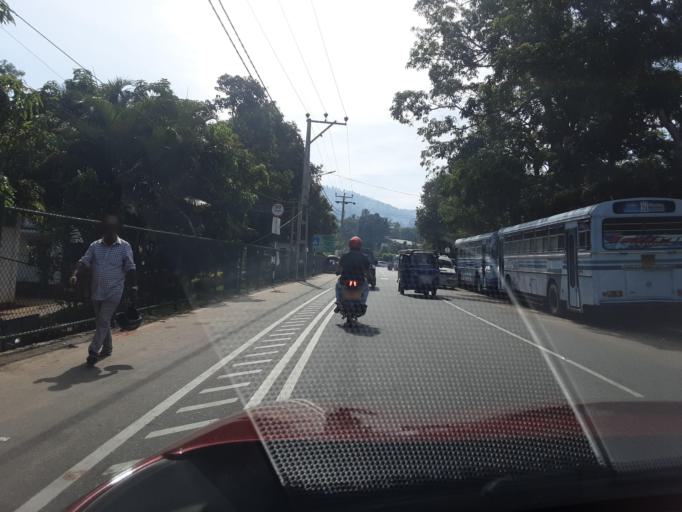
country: LK
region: Uva
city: Badulla
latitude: 6.9842
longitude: 81.0658
